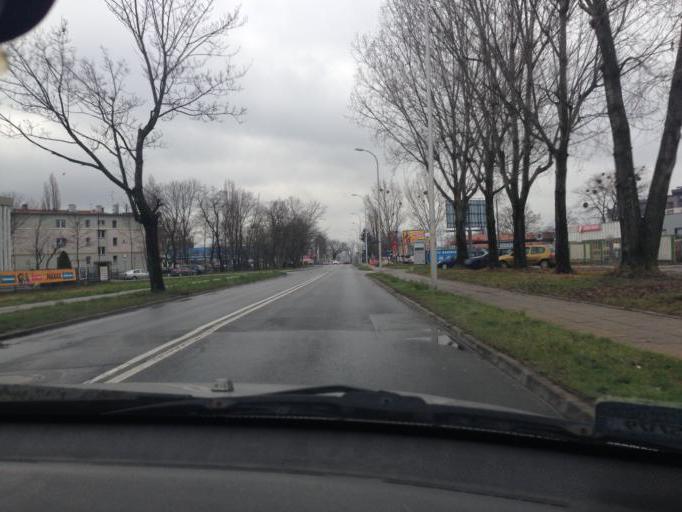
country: PL
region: Opole Voivodeship
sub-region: Powiat opolski
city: Opole
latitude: 50.6822
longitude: 17.9407
